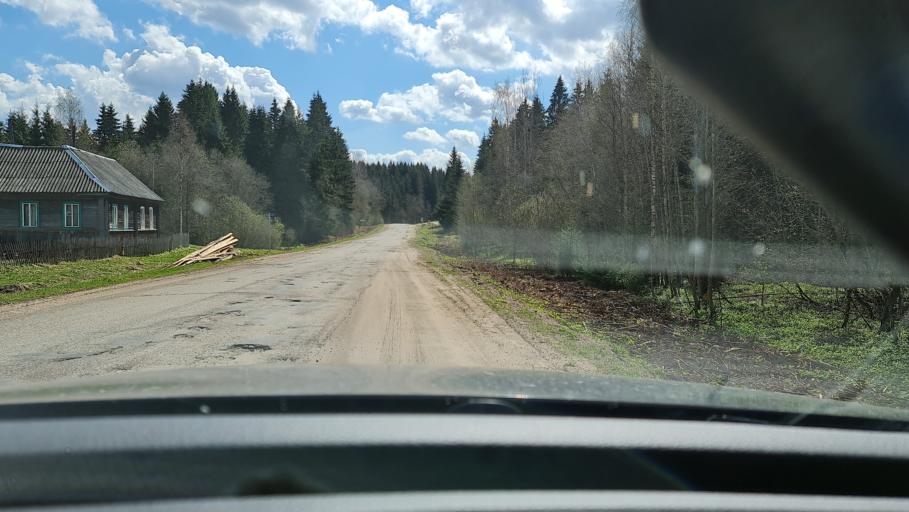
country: RU
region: Tverskaya
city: Toropets
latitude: 56.6408
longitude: 31.4227
